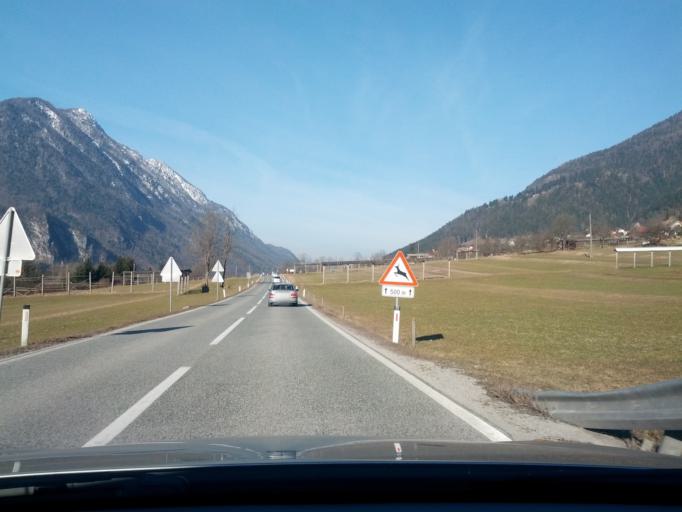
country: SI
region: Jesenice
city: Hrusica
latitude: 46.4640
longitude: 13.9562
